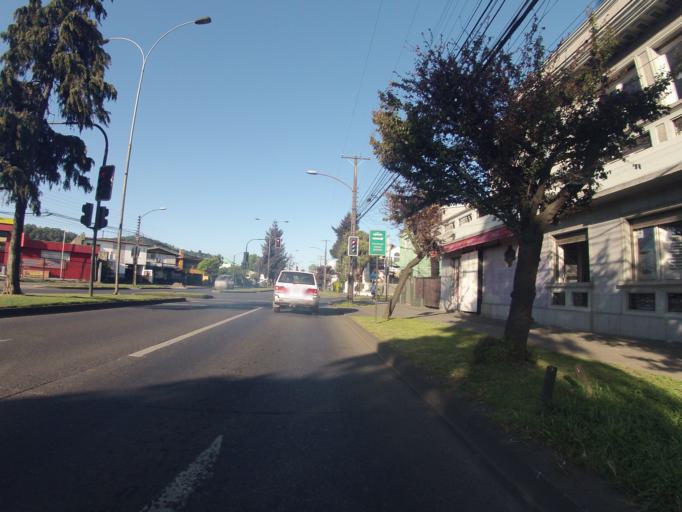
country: CL
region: Araucania
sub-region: Provincia de Cautin
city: Temuco
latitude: -38.7368
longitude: -72.5954
